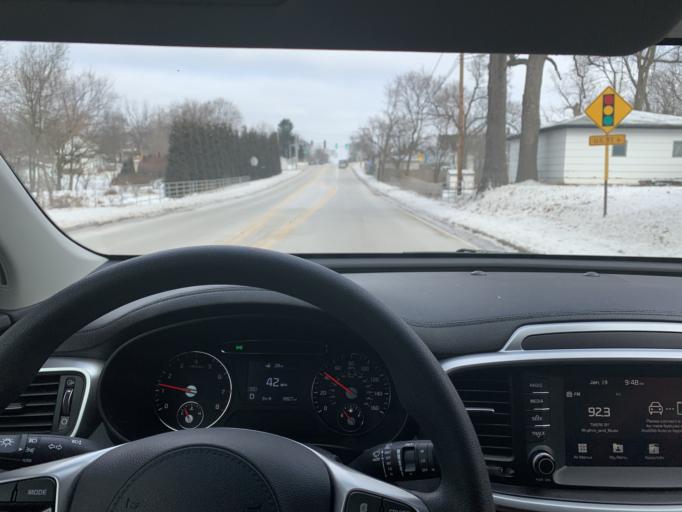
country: US
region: Illinois
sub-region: Will County
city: Ingalls Park
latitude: 41.5396
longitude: -88.0436
